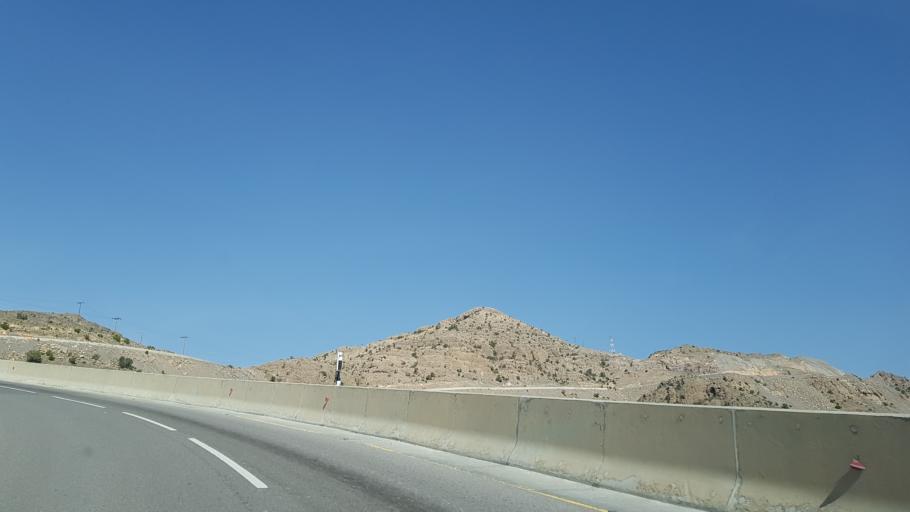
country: OM
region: Muhafazat ad Dakhiliyah
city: Izki
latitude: 23.0649
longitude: 57.7199
